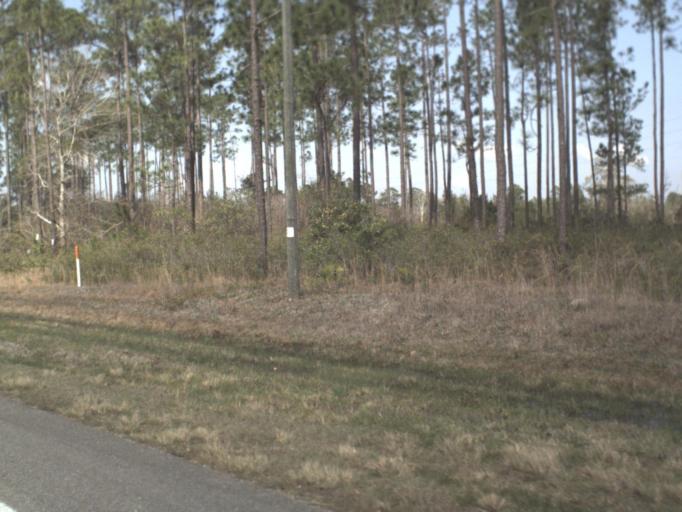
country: US
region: Florida
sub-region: Gadsden County
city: Gretna
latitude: 30.3838
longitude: -84.7272
